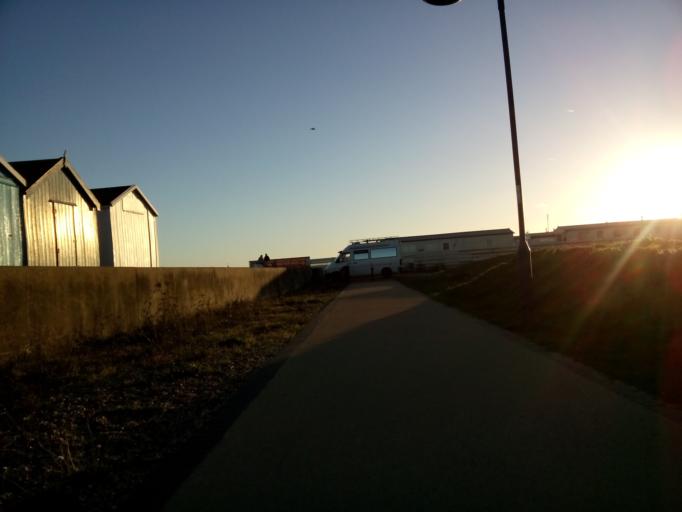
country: GB
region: England
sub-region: Suffolk
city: Felixstowe
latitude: 51.9470
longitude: 1.3341
